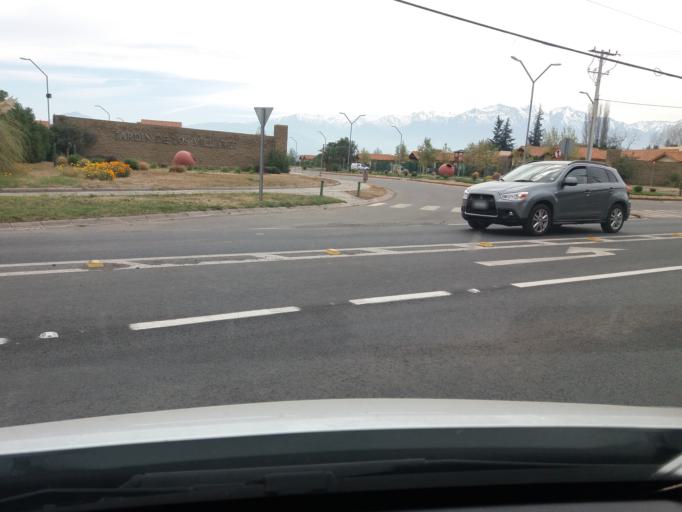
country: CL
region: Valparaiso
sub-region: Provincia de Los Andes
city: Los Andes
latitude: -32.8321
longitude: -70.6225
